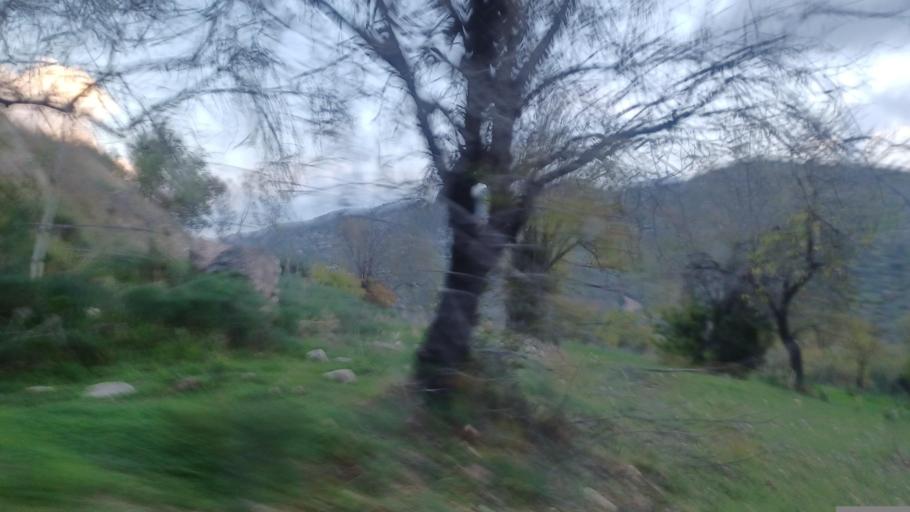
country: CY
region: Pafos
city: Mesogi
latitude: 34.7906
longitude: 32.5267
